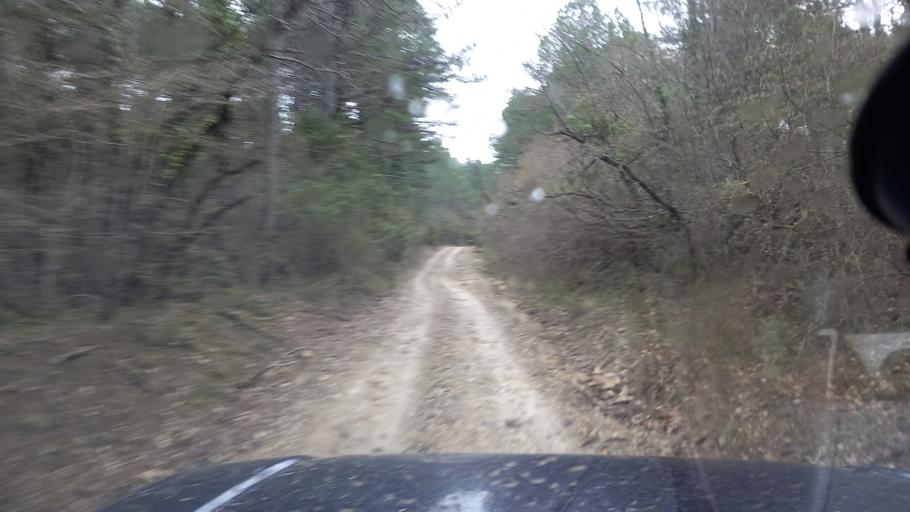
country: RU
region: Krasnodarskiy
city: Arkhipo-Osipovka
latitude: 44.3753
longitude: 38.4607
